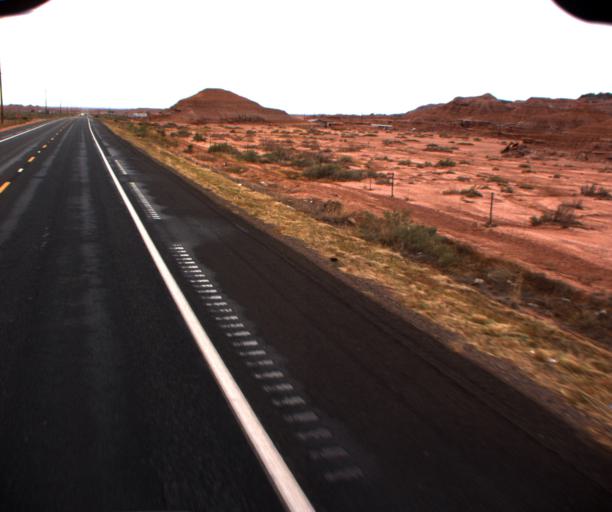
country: US
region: Arizona
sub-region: Coconino County
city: Tuba City
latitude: 36.1066
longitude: -111.2565
